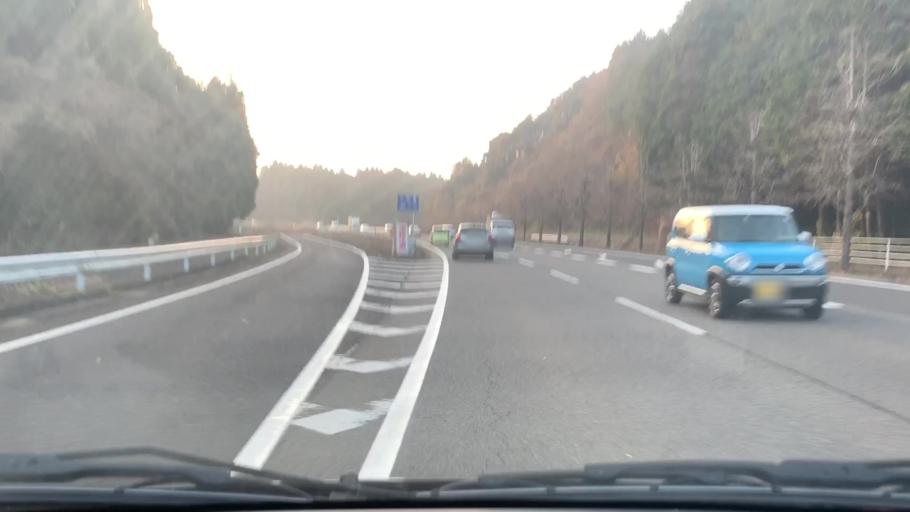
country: JP
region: Saga Prefecture
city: Imaricho-ko
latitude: 33.2660
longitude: 129.9550
